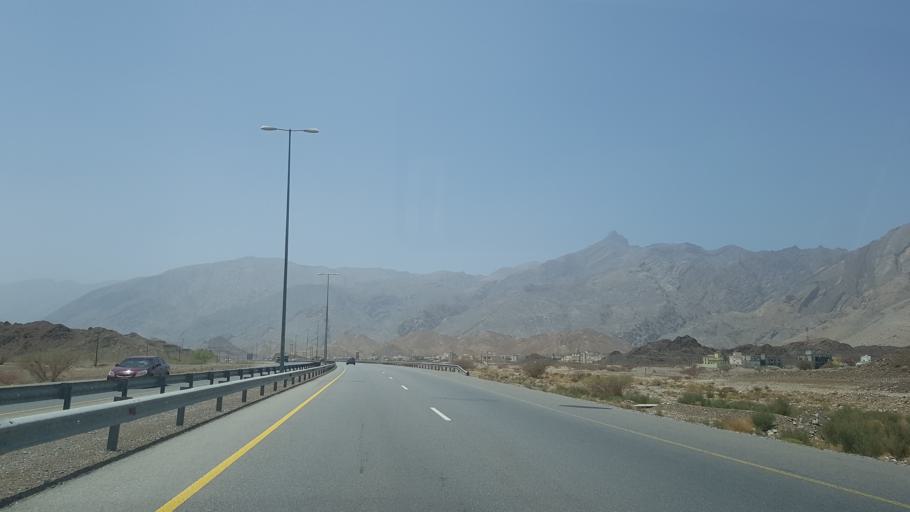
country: OM
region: Muhafazat ad Dakhiliyah
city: Sufalat Sama'il
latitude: 23.3266
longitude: 57.9702
